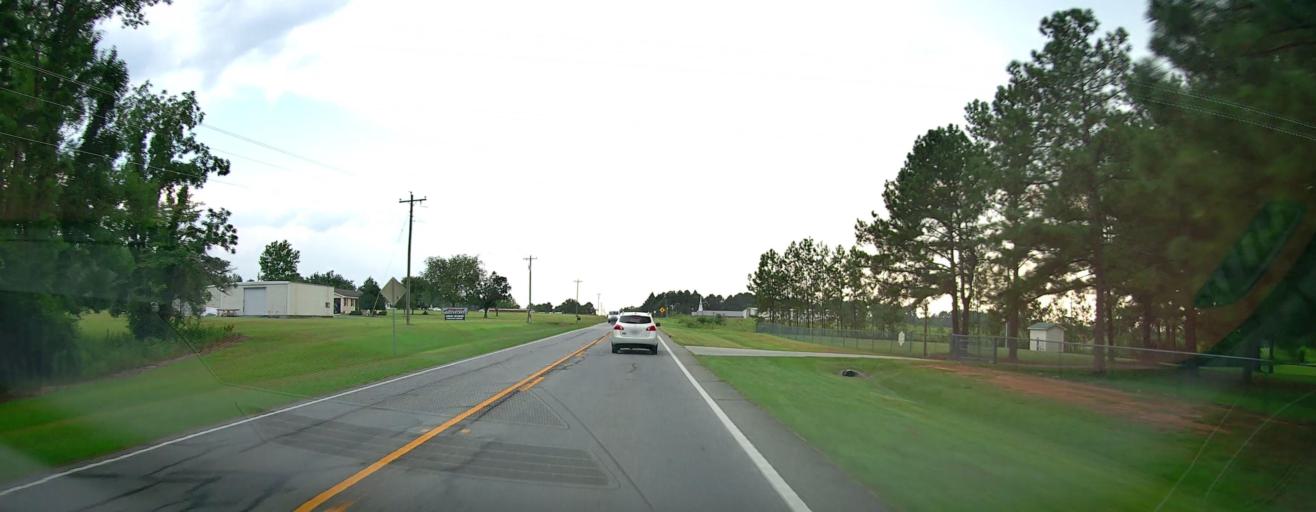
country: US
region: Georgia
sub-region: Laurens County
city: East Dublin
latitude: 32.5676
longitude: -82.8450
